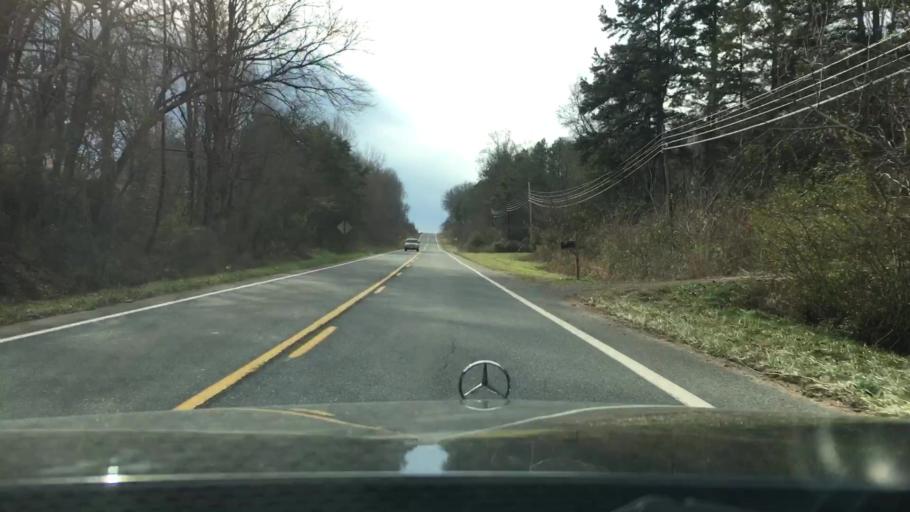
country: US
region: Virginia
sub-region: Pittsylvania County
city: Motley
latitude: 37.0871
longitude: -79.3233
